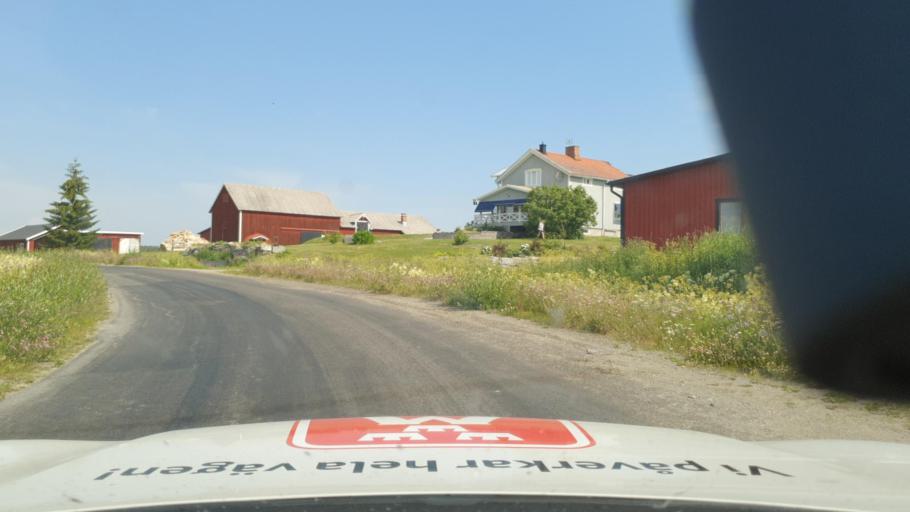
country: SE
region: Vaesterbotten
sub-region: Skelleftea Kommun
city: Burtraesk
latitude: 64.5183
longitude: 20.6297
